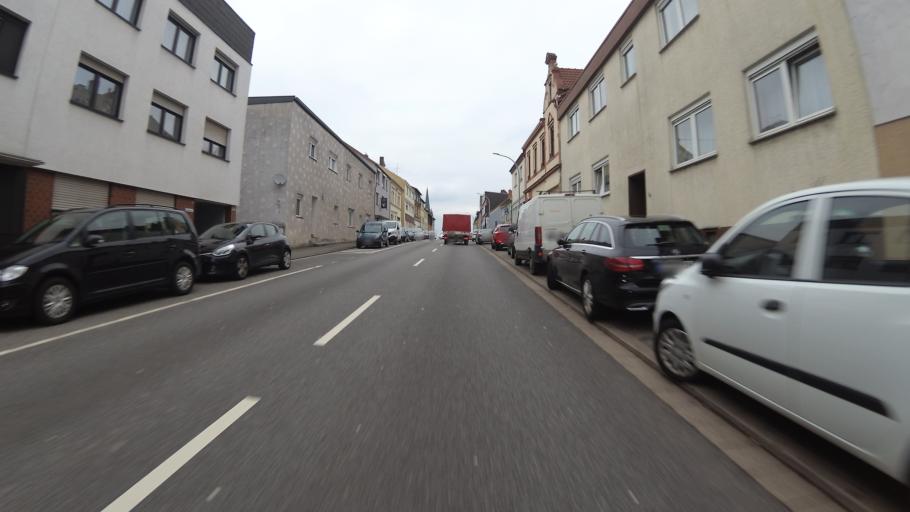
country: DE
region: Saarland
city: Spiesen-Elversberg
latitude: 49.3112
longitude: 7.1262
